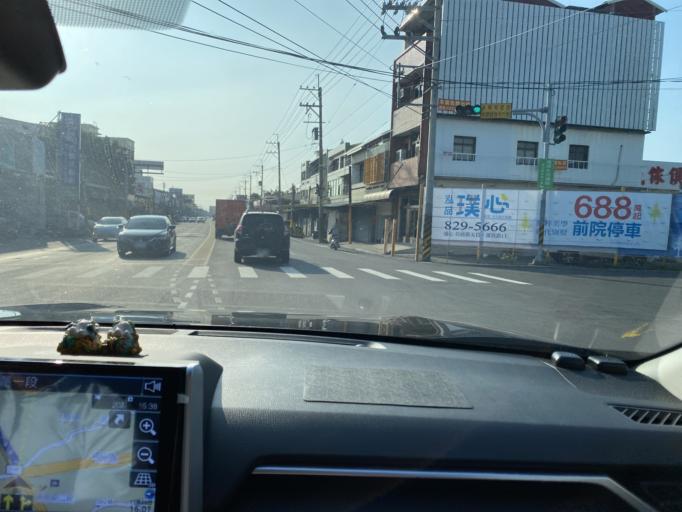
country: TW
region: Taiwan
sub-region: Changhua
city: Chang-hua
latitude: 23.9517
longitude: 120.5376
